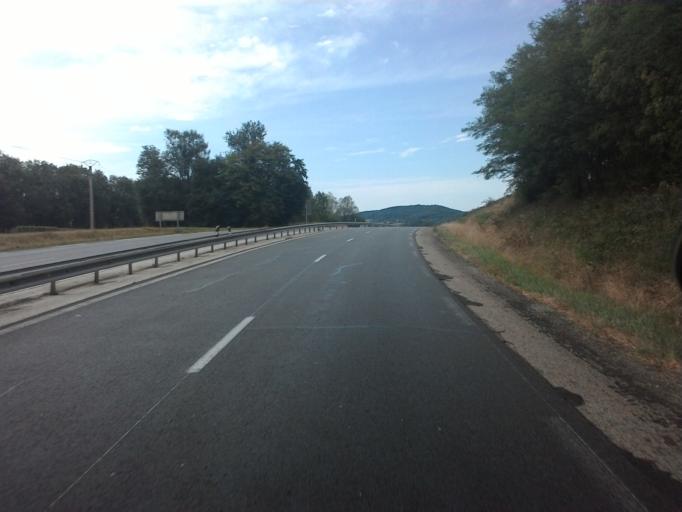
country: FR
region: Franche-Comte
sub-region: Departement du Jura
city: Montmorot
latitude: 46.7512
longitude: 5.5580
